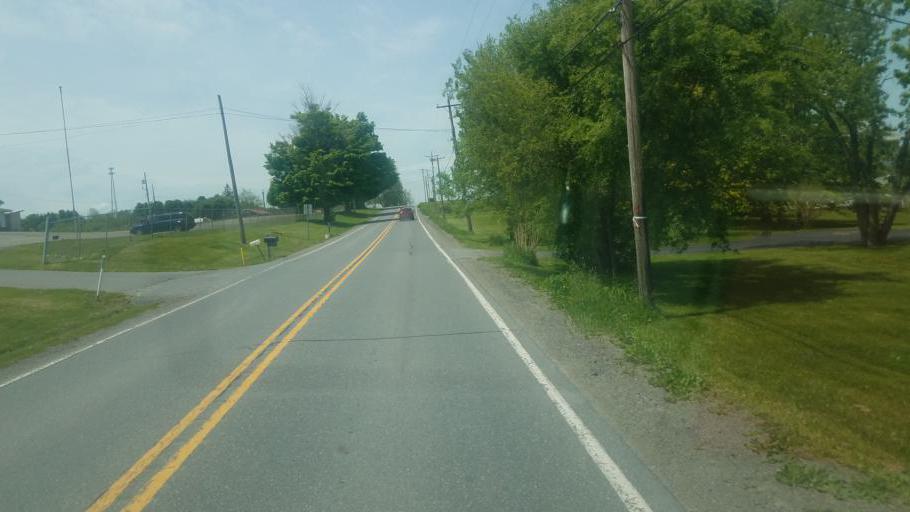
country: US
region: Pennsylvania
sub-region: Tioga County
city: Wellsboro
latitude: 41.7700
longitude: -77.2045
